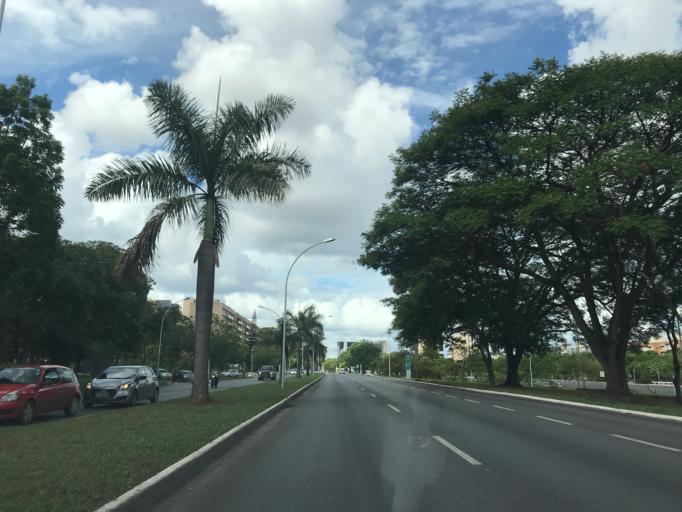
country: BR
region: Federal District
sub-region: Brasilia
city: Brasilia
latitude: -15.8091
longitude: -47.8929
